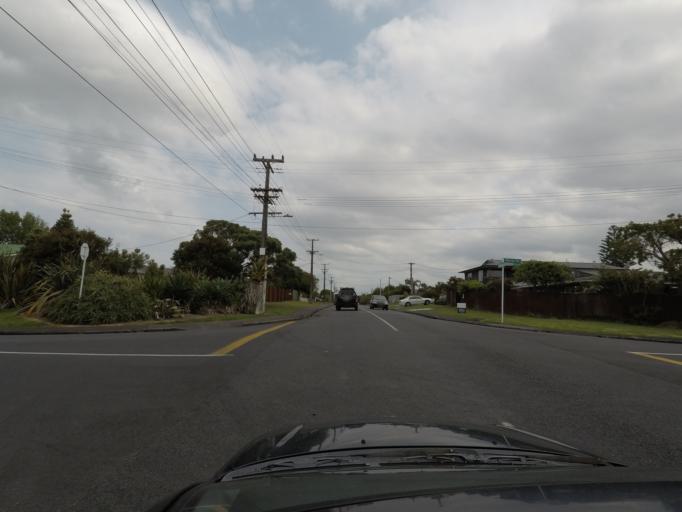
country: NZ
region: Auckland
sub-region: Auckland
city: Rosebank
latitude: -36.8268
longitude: 174.6464
